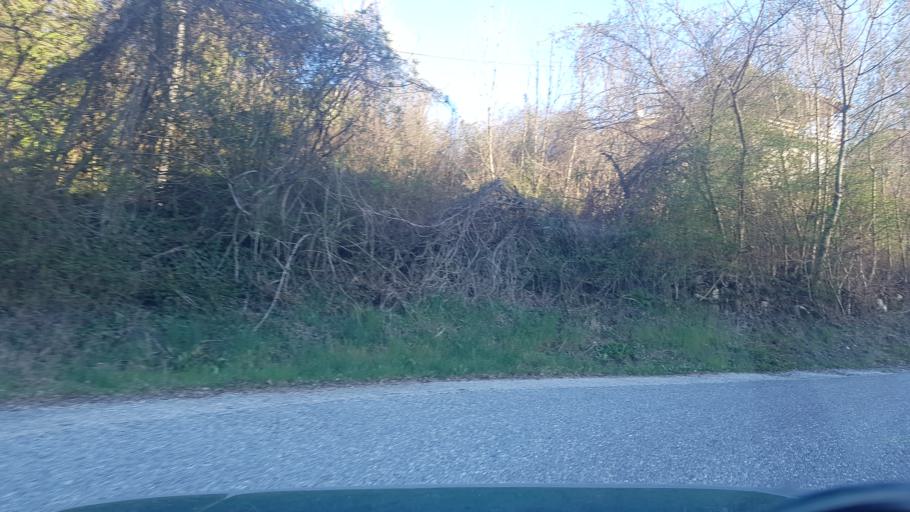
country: SI
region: Kanal
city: Kanal
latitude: 46.0767
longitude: 13.6334
